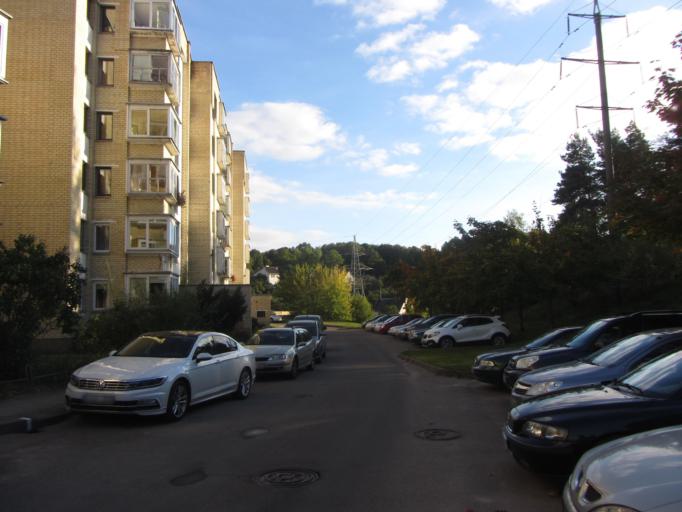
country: LT
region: Vilnius County
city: Lazdynai
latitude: 54.6421
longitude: 25.2086
